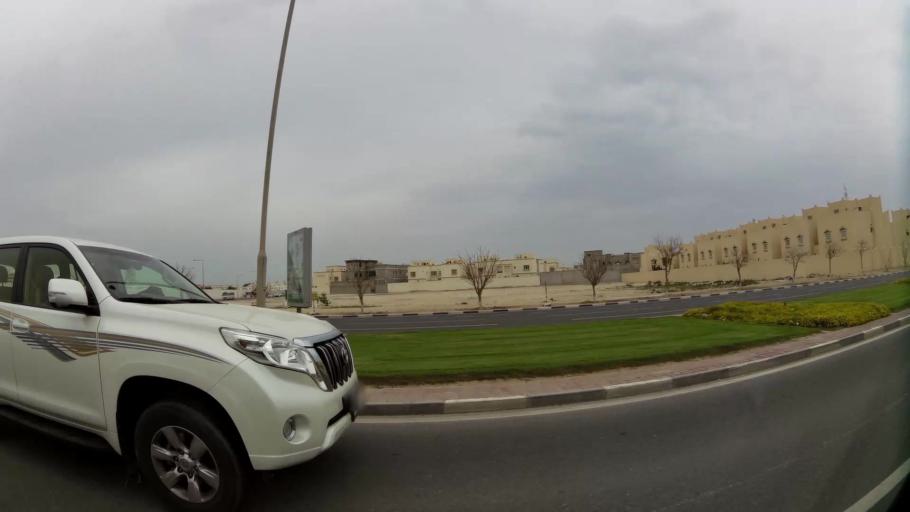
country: QA
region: Baladiyat ad Dawhah
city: Doha
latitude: 25.3302
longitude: 51.4829
